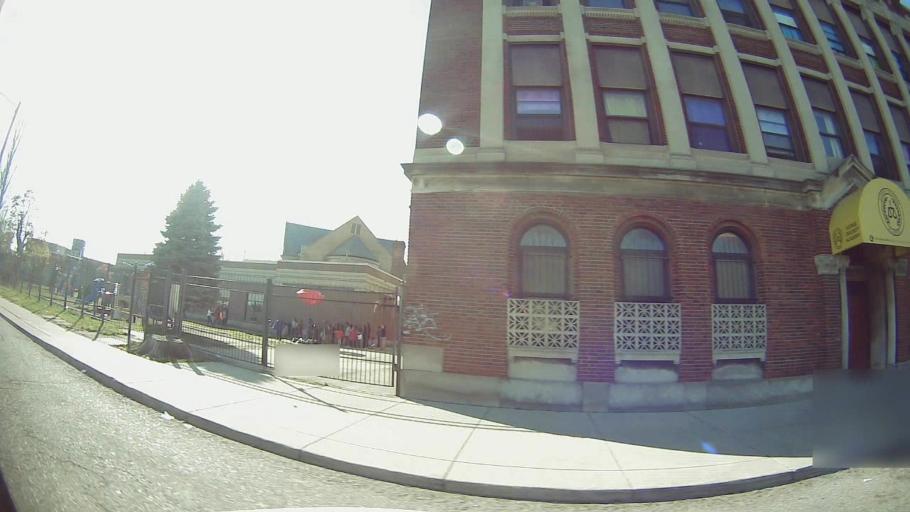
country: US
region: Michigan
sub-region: Wayne County
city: Detroit
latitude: 42.3491
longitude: -83.0867
